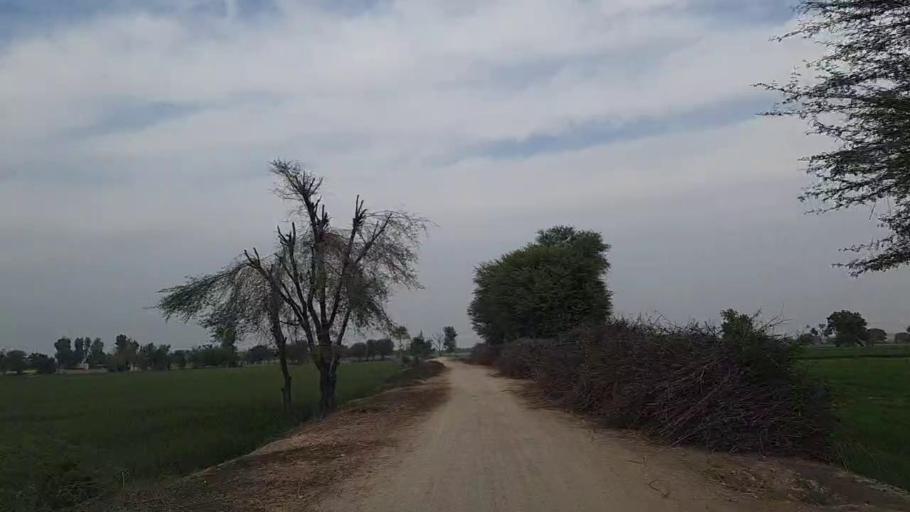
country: PK
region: Sindh
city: Daur
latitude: 26.4393
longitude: 68.4709
